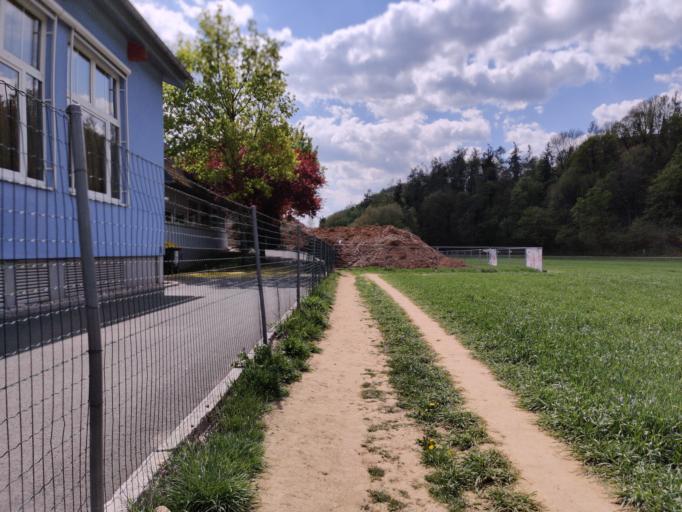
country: AT
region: Styria
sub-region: Graz Stadt
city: Wetzelsdorf
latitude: 47.0383
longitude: 15.3915
